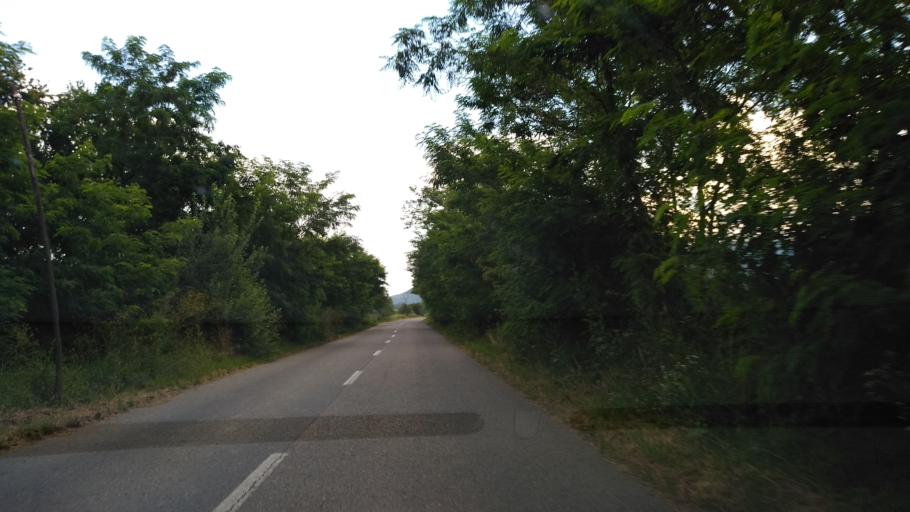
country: RO
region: Hunedoara
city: Salasu de Sus
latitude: 45.5152
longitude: 22.9577
